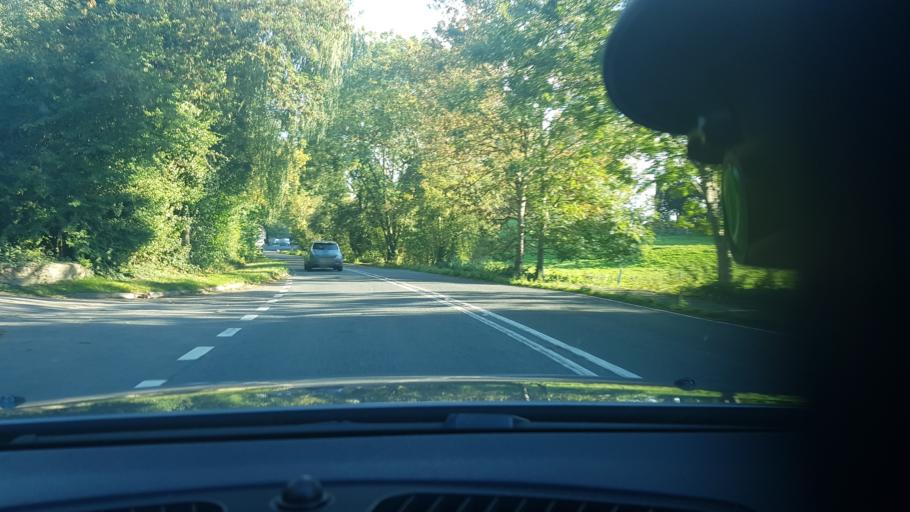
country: GB
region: England
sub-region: Gloucestershire
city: Cirencester
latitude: 51.7699
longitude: -1.9739
